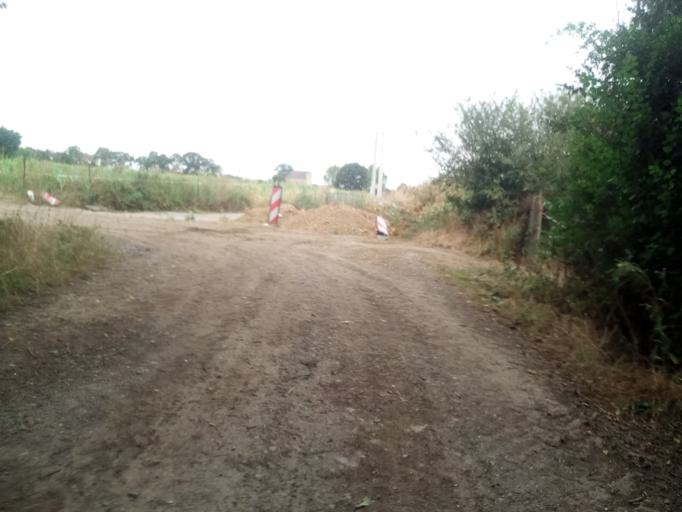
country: FR
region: Lower Normandy
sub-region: Departement du Calvados
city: Clinchamps-sur-Orne
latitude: 49.0451
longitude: -0.4001
